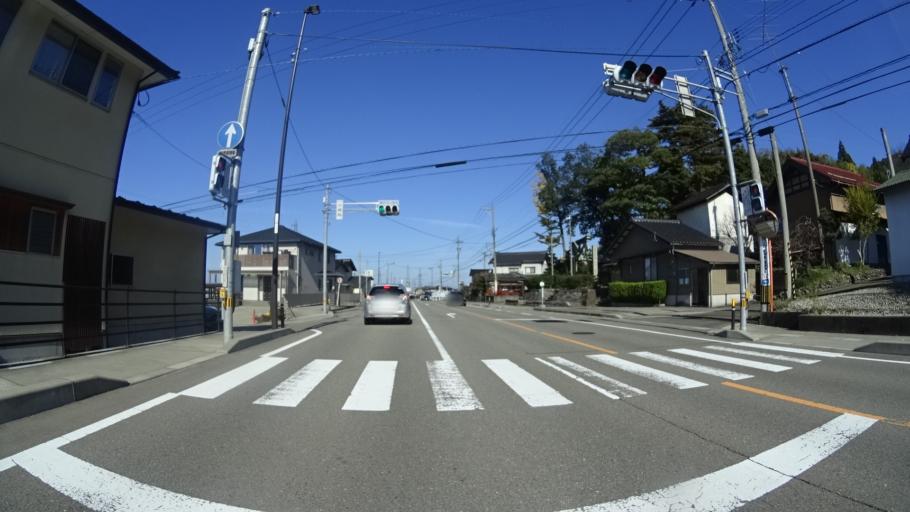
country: JP
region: Ishikawa
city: Tsurugi-asahimachi
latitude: 36.4724
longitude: 136.6164
